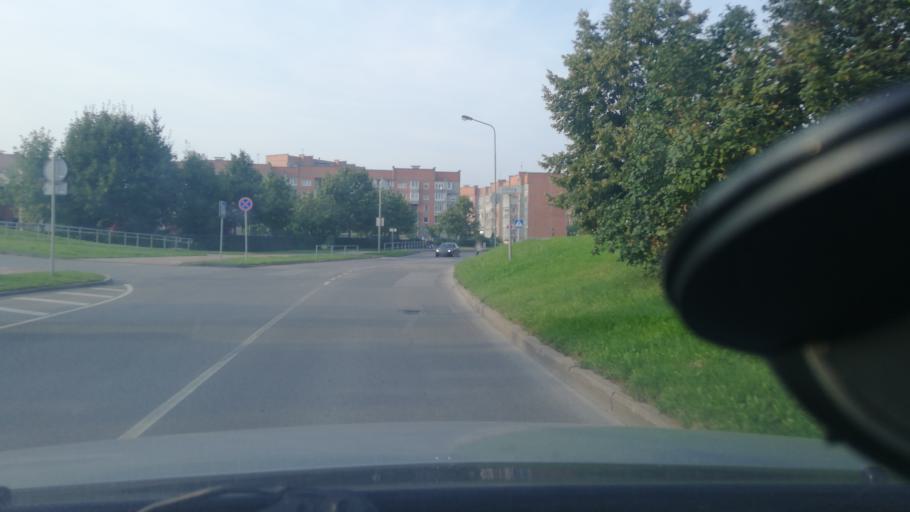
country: LT
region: Klaipedos apskritis
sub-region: Klaipeda
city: Klaipeda
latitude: 55.6639
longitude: 21.2004
